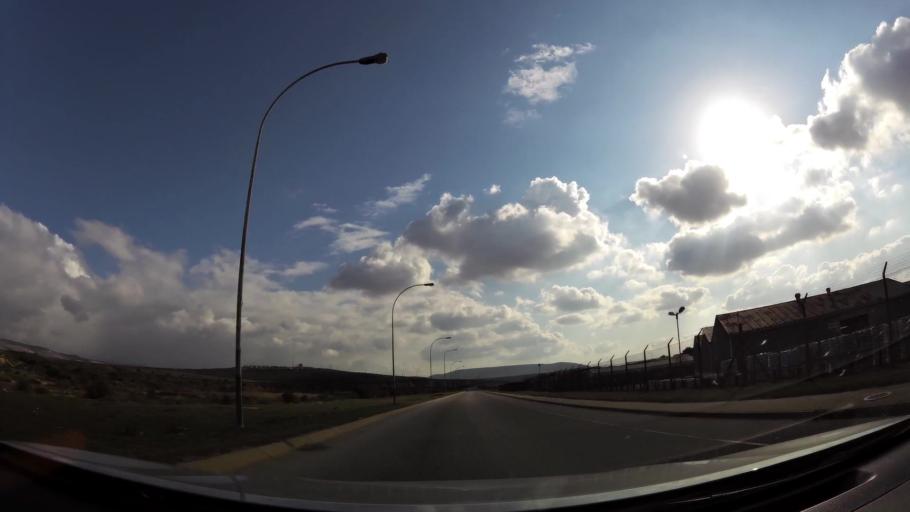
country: ZA
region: Eastern Cape
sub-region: Nelson Mandela Bay Metropolitan Municipality
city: Uitenhage
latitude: -33.7911
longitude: 25.4152
